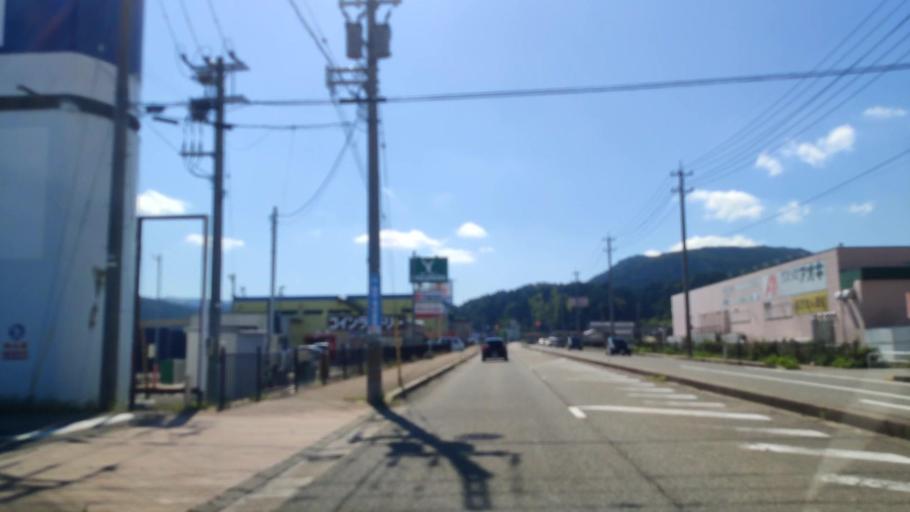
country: JP
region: Ishikawa
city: Nanao
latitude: 37.3870
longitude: 136.9026
